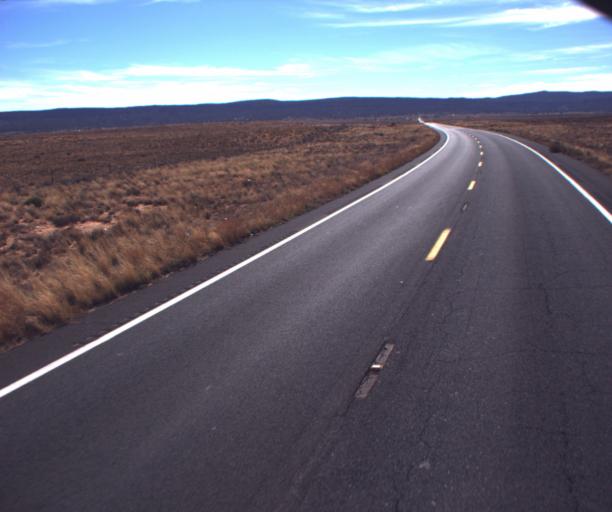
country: US
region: Arizona
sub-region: Coconino County
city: Kaibito
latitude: 36.4842
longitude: -110.7049
